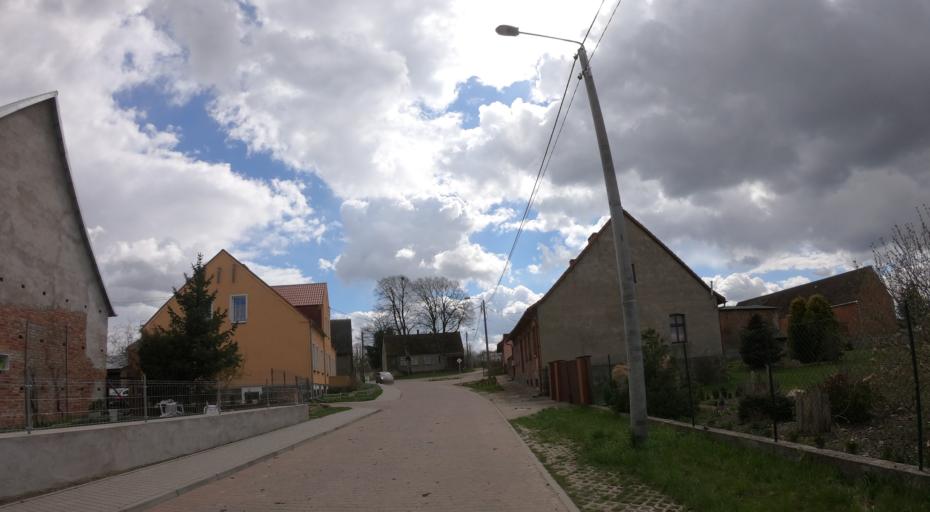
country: PL
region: West Pomeranian Voivodeship
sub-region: Powiat drawski
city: Drawsko Pomorskie
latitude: 53.5402
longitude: 15.8697
